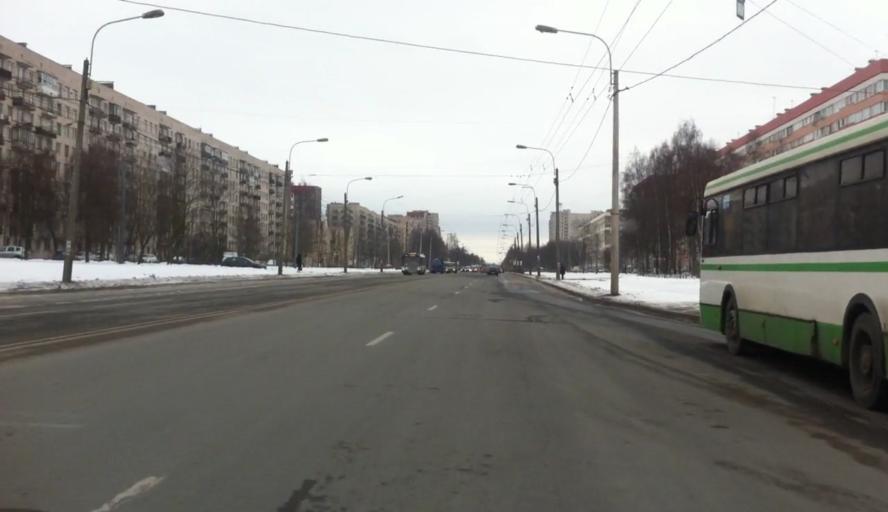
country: RU
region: St.-Petersburg
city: Uritsk
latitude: 59.8418
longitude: 30.1754
